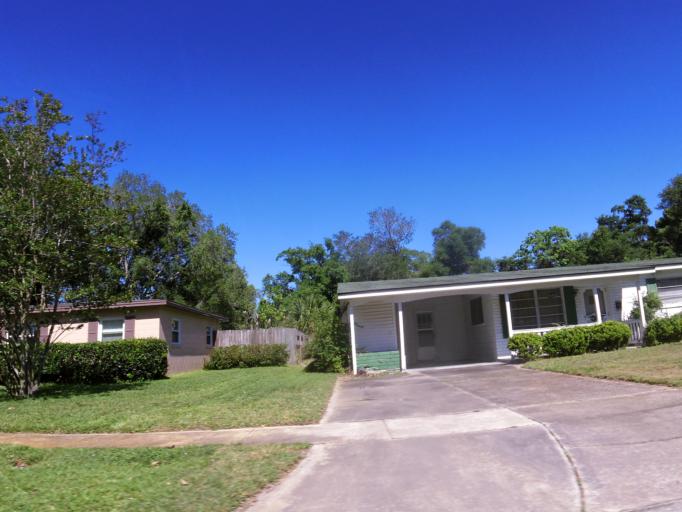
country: US
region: Florida
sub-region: Duval County
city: Jacksonville
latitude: 30.3464
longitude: -81.5686
